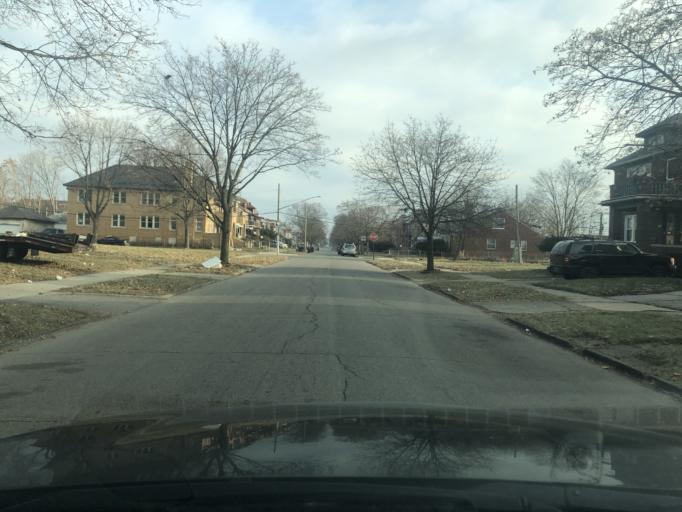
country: US
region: Michigan
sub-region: Wayne County
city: Highland Park
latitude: 42.3926
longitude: -83.1260
